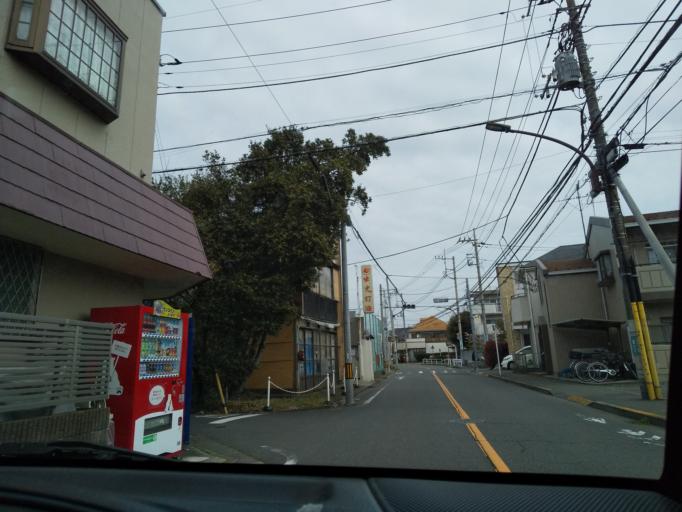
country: JP
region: Tokyo
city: Kokubunji
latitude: 35.6832
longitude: 139.4569
